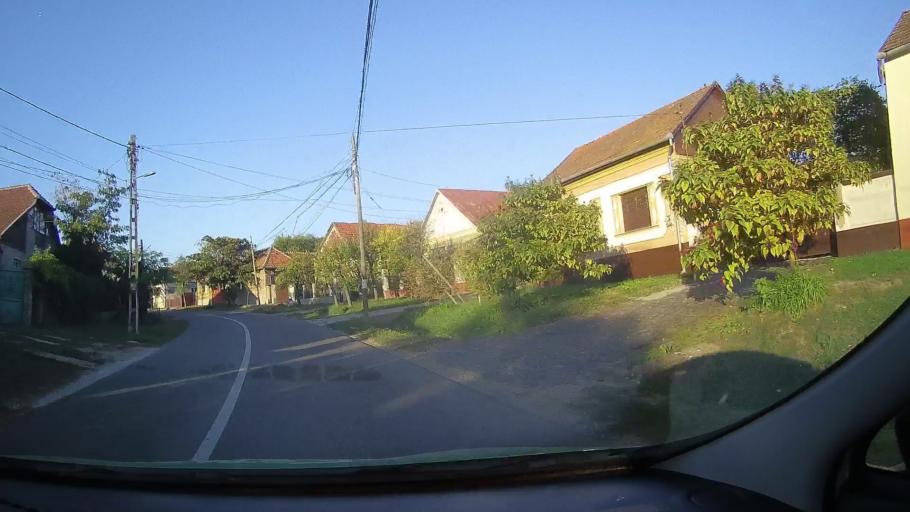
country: RO
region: Bihor
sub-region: Comuna Cetariu
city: Cetariu
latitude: 47.1384
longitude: 21.9980
